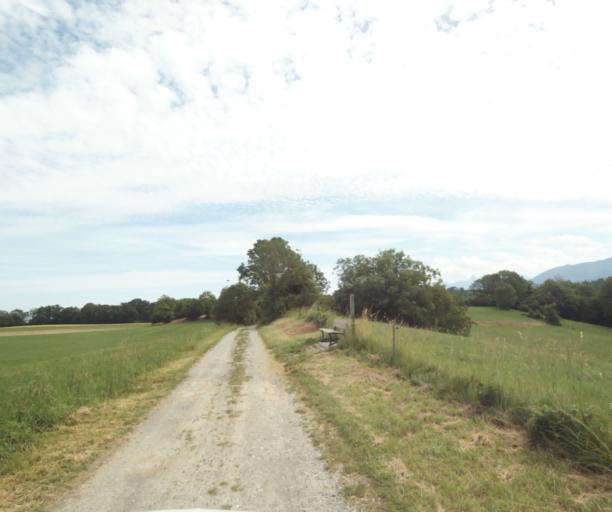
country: FR
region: Rhone-Alpes
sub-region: Departement de la Haute-Savoie
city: Margencel
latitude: 46.3419
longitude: 6.4274
